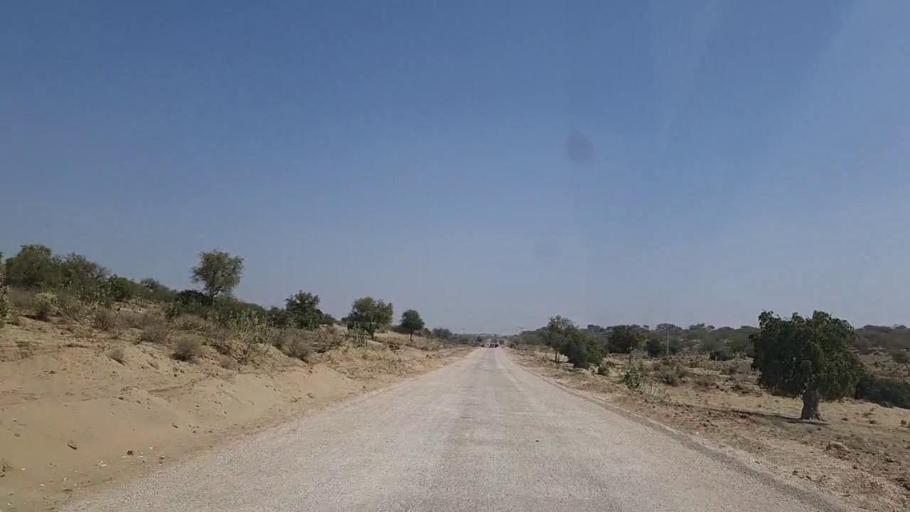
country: PK
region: Sindh
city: Diplo
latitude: 24.4784
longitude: 69.5097
